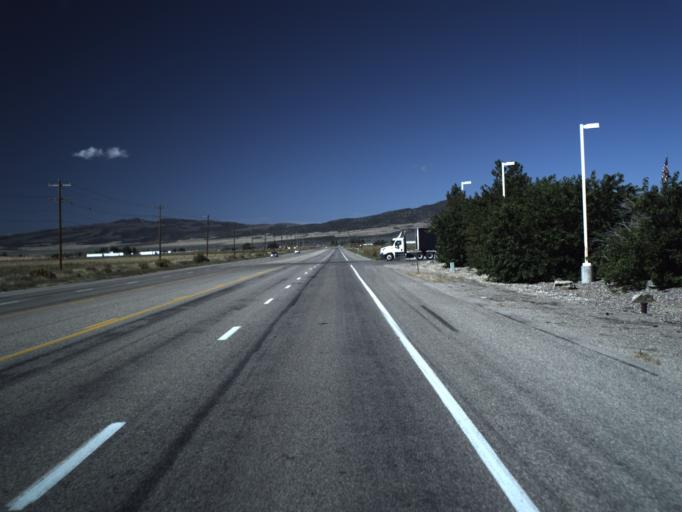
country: US
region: Utah
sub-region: Iron County
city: Cedar City
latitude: 37.6850
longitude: -113.1494
